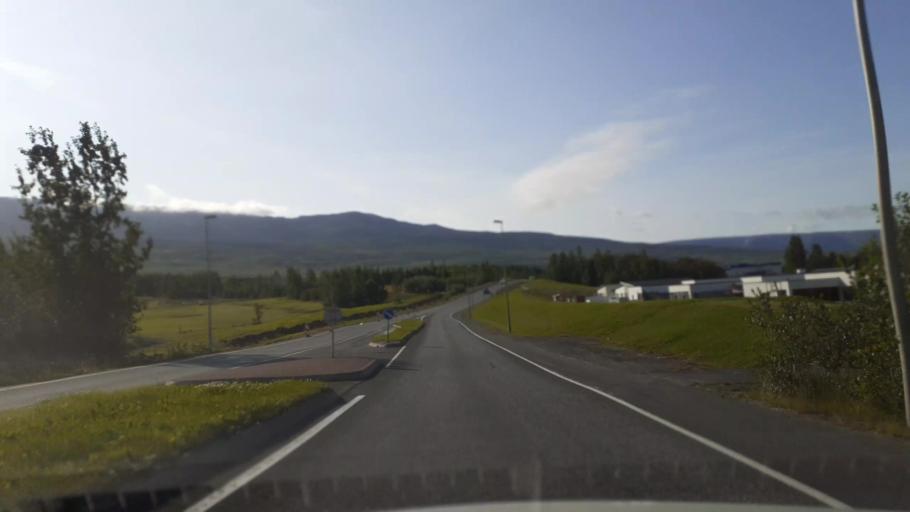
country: IS
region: Northeast
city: Akureyri
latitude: 65.6717
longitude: -18.1181
